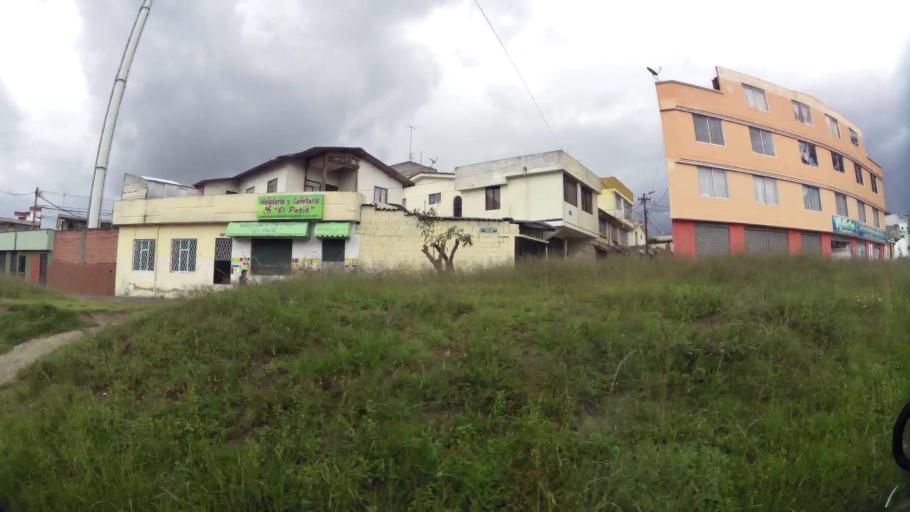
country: EC
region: Pichincha
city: Quito
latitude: -0.0874
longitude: -78.4759
